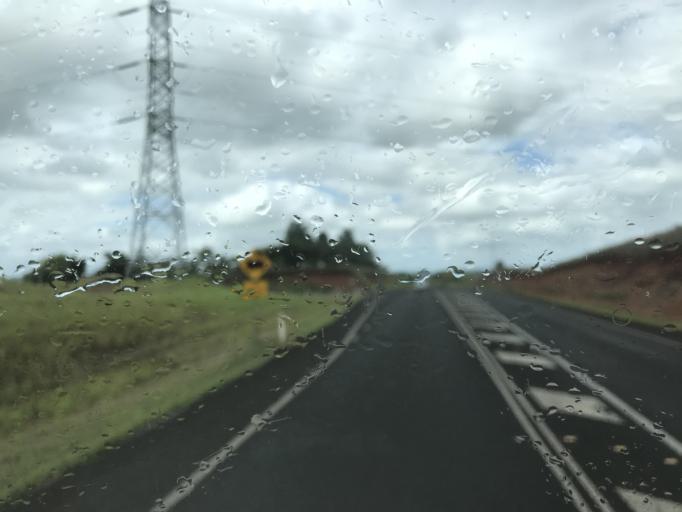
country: AU
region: Queensland
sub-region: Cassowary Coast
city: Innisfail
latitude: -17.5790
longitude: 145.9865
